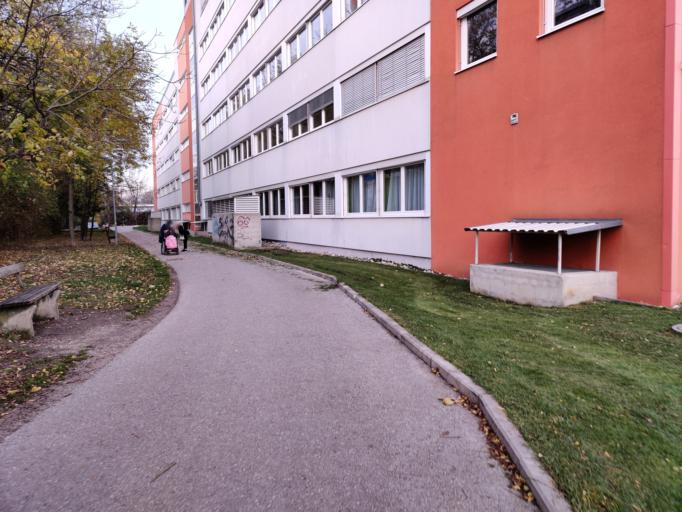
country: AT
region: Lower Austria
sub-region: Sankt Polten Stadt
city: Sankt Poelten
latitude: 48.2121
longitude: 15.6298
